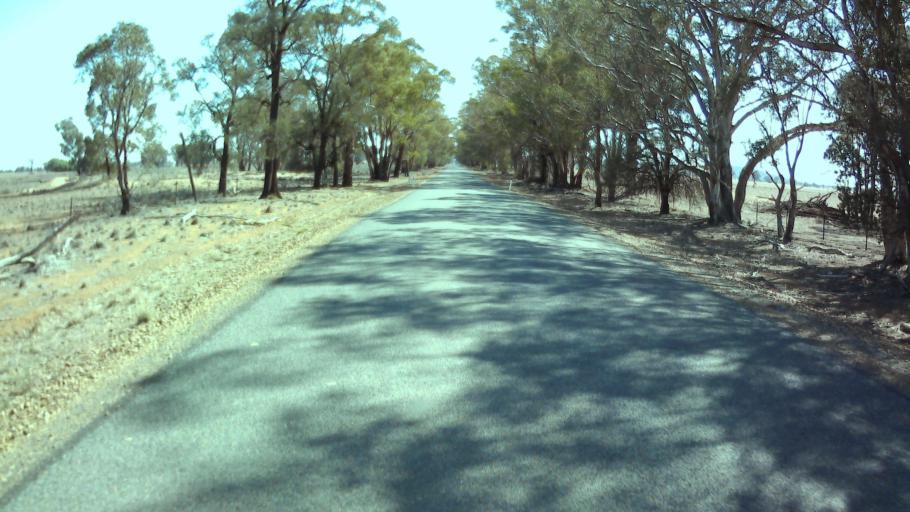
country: AU
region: New South Wales
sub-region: Weddin
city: Grenfell
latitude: -33.7258
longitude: 147.8939
